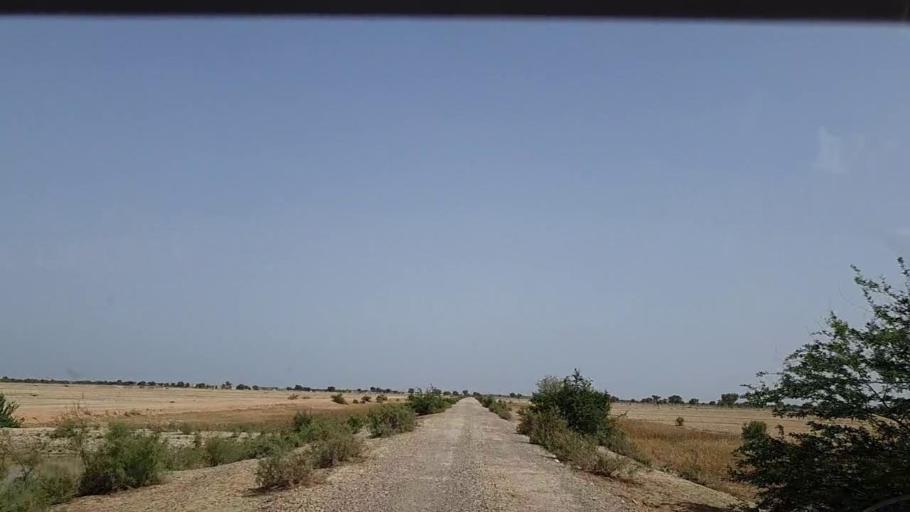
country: PK
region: Sindh
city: Johi
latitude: 26.7588
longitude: 67.6652
